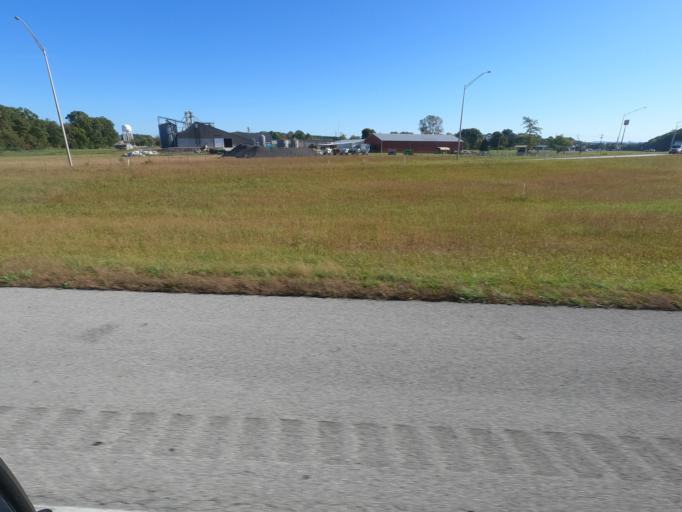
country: US
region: Tennessee
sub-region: Coffee County
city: Manchester
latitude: 35.4926
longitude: -86.0758
